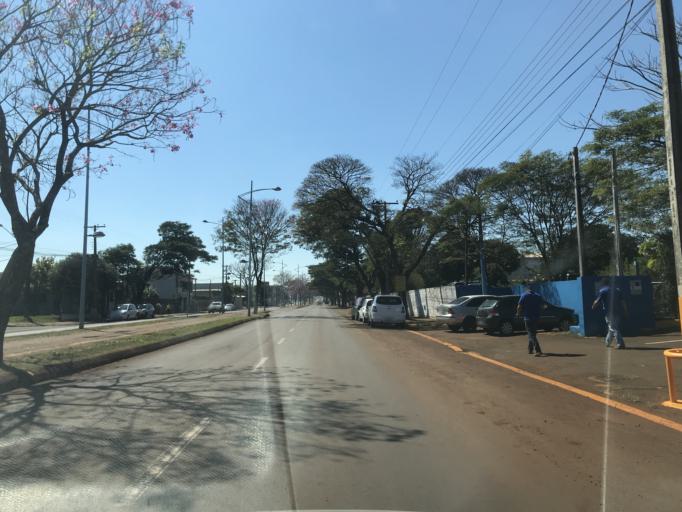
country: BR
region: Parana
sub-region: Toledo
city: Toledo
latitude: -24.7227
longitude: -53.7198
